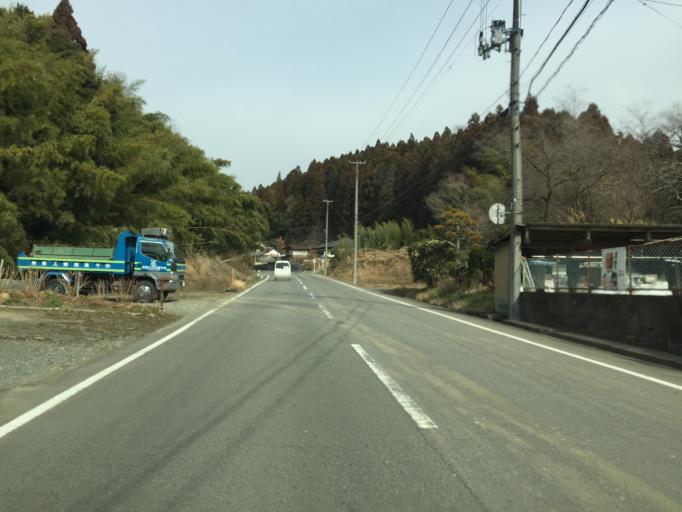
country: JP
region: Fukushima
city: Iwaki
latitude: 37.0083
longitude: 140.8159
